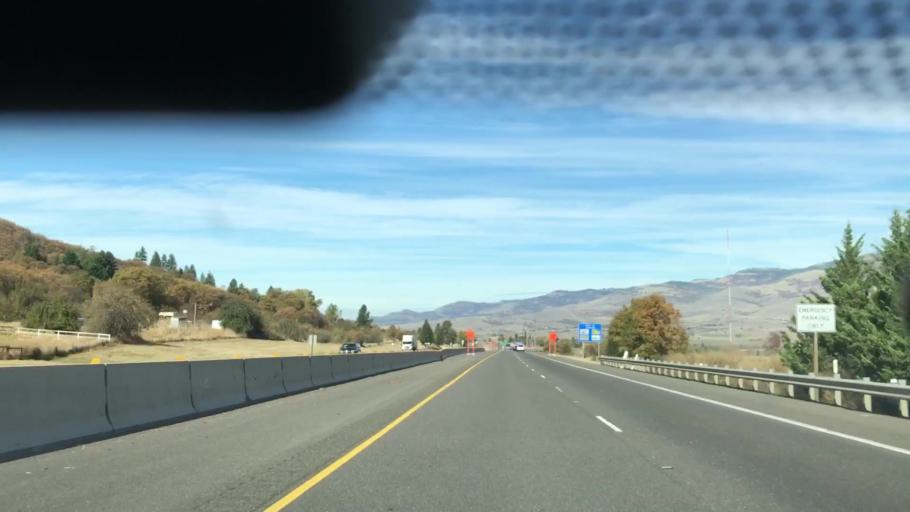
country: US
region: Oregon
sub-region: Jackson County
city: Ashland
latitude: 42.1587
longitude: -122.6482
